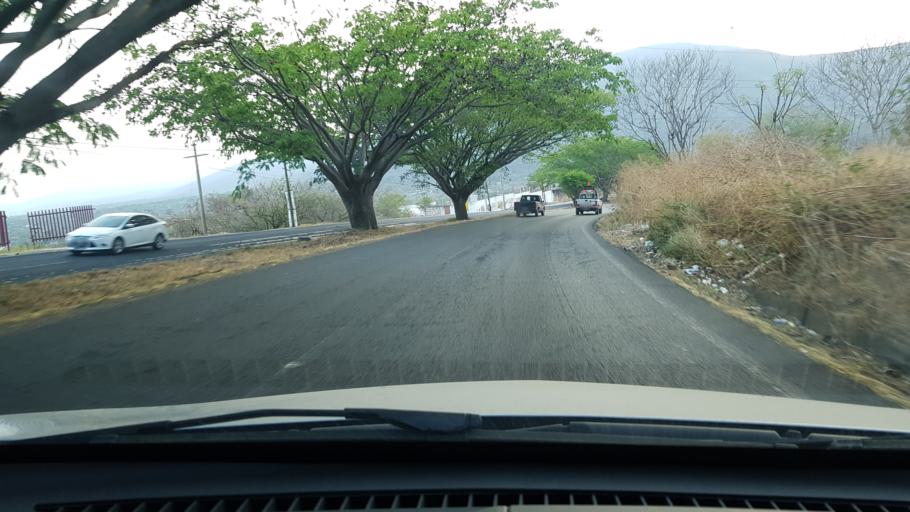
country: MX
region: Morelos
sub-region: Jiutepec
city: Independencia
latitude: 18.8604
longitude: -99.0977
